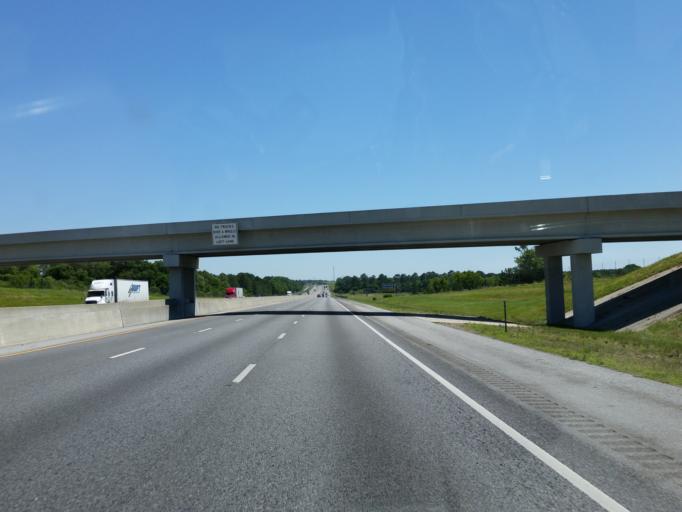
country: US
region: Georgia
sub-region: Turner County
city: Ashburn
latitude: 31.6092
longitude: -83.5653
